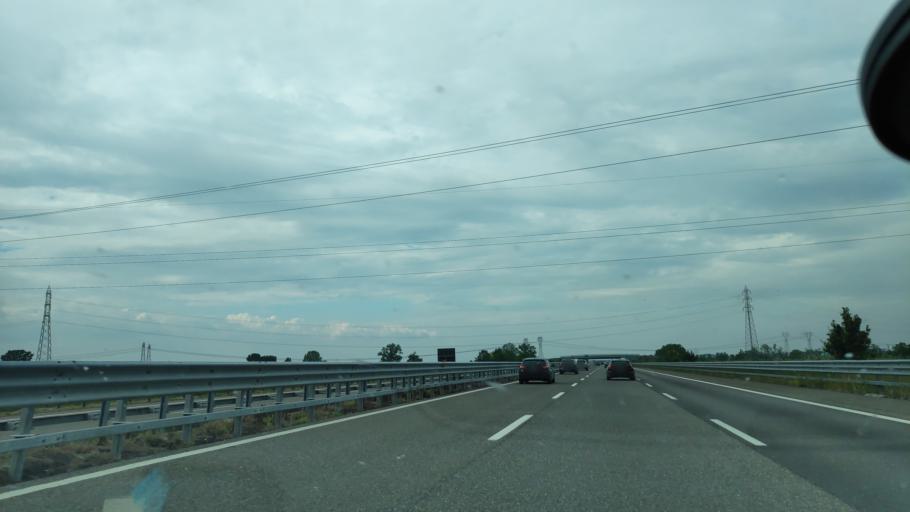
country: IT
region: Piedmont
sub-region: Provincia di Alessandria
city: Castelnuovo Scrivia
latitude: 44.9850
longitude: 8.9030
